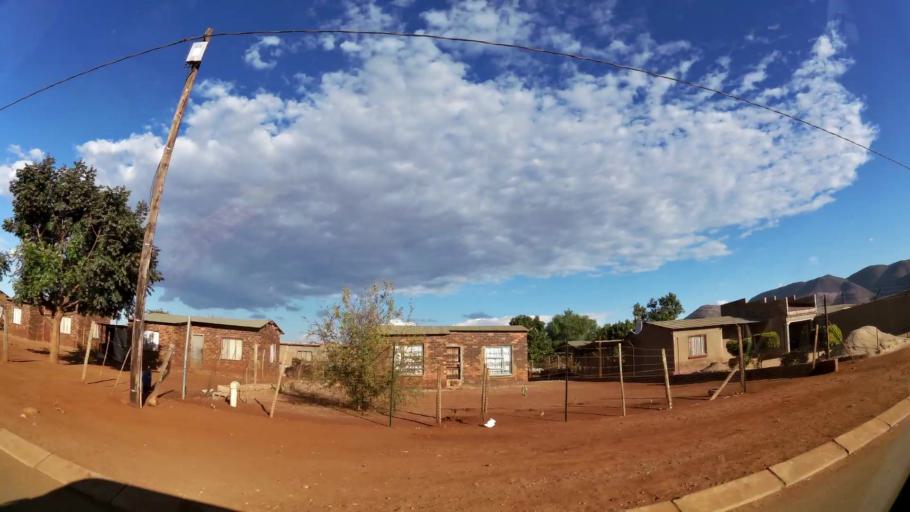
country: ZA
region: Limpopo
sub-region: Waterberg District Municipality
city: Mokopane
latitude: -24.1844
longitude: 28.9706
